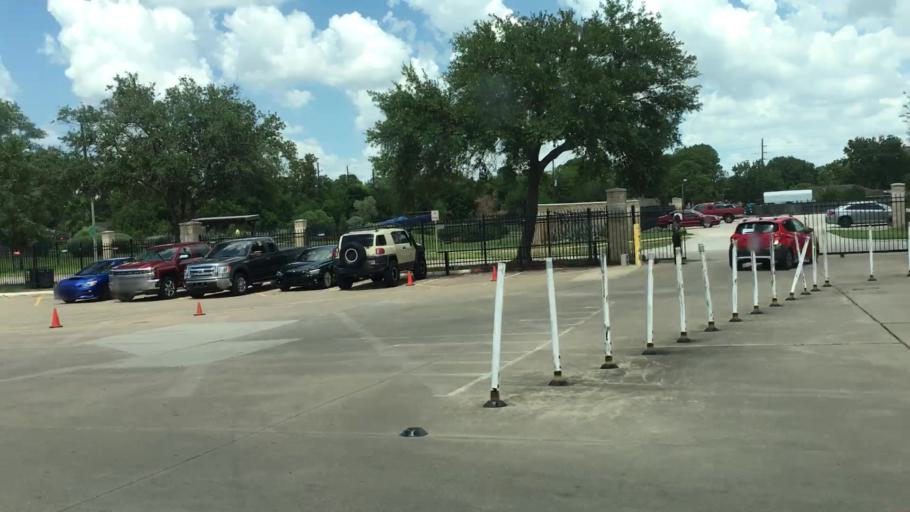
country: US
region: Texas
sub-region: Fort Bend County
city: Meadows Place
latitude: 29.6495
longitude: -95.5757
